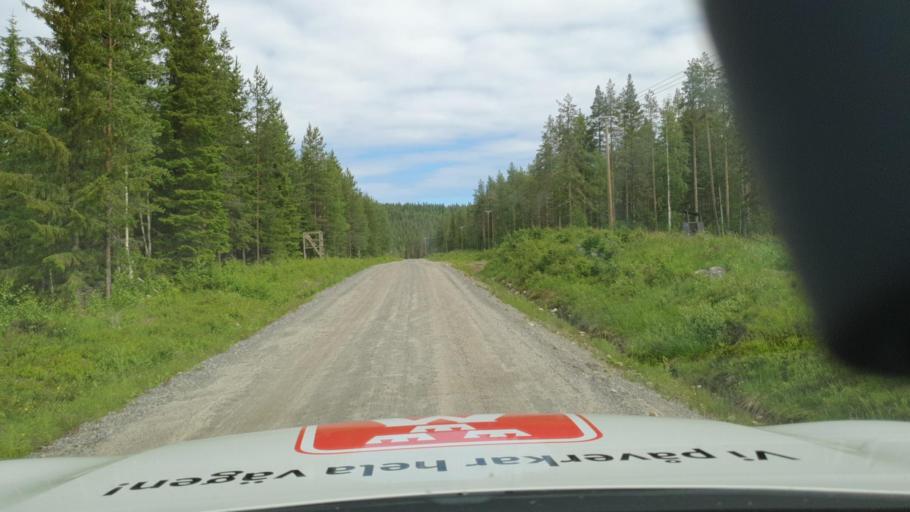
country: SE
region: Vaesterbotten
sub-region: Skelleftea Kommun
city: Langsele
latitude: 64.5815
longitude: 20.2964
